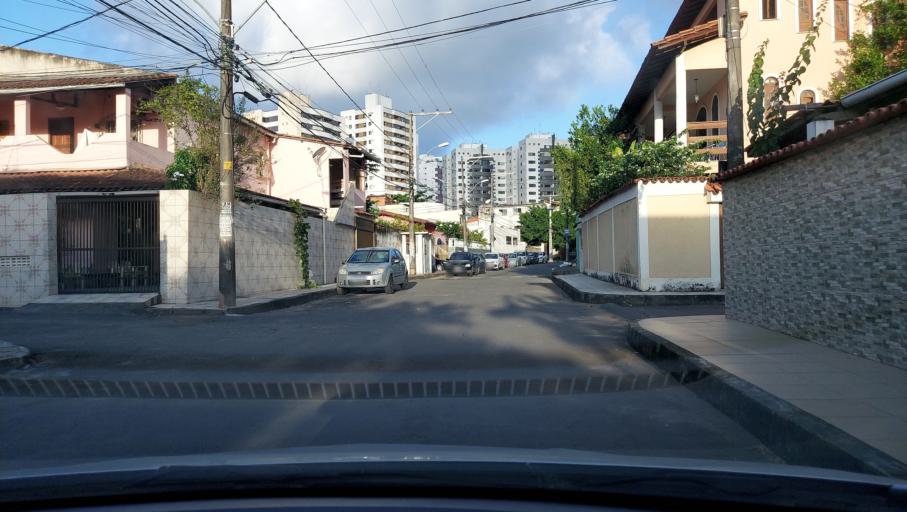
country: BR
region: Bahia
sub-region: Salvador
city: Salvador
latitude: -12.9843
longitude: -38.4459
